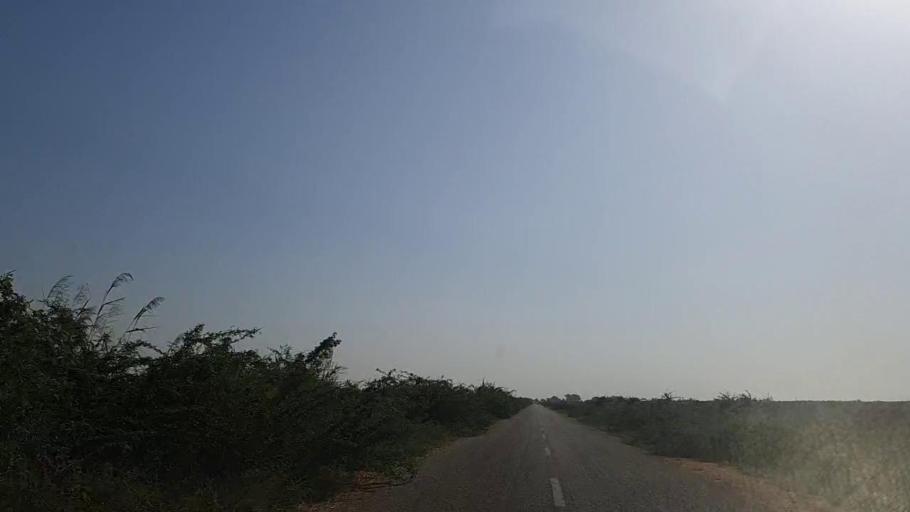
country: PK
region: Sindh
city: Jati
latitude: 24.4351
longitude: 68.2600
